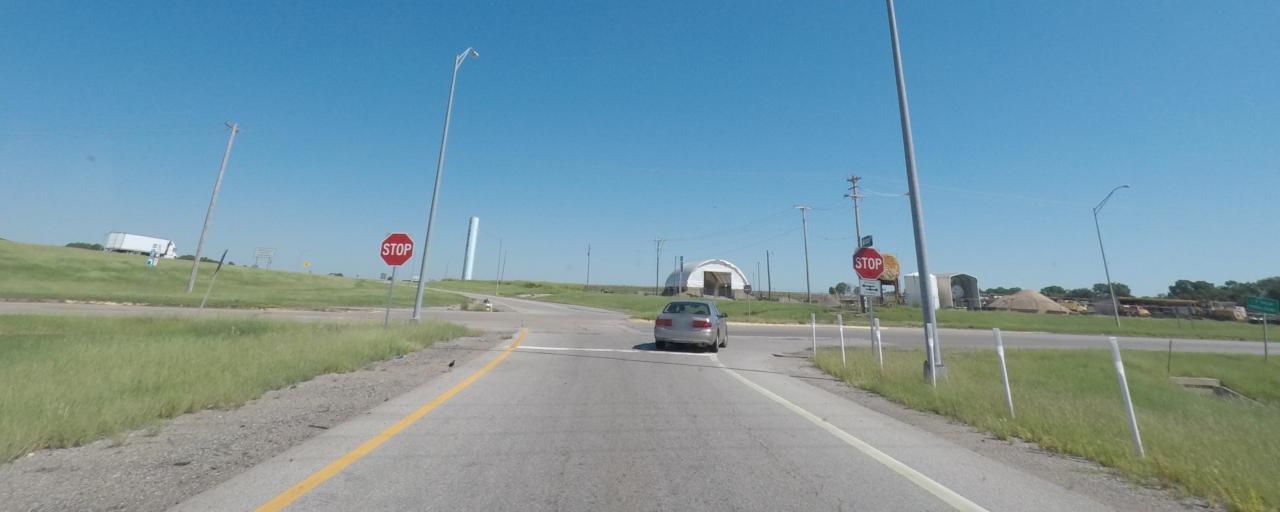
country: US
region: Oklahoma
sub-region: Kay County
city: Tonkawa
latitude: 36.6948
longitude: -97.3451
